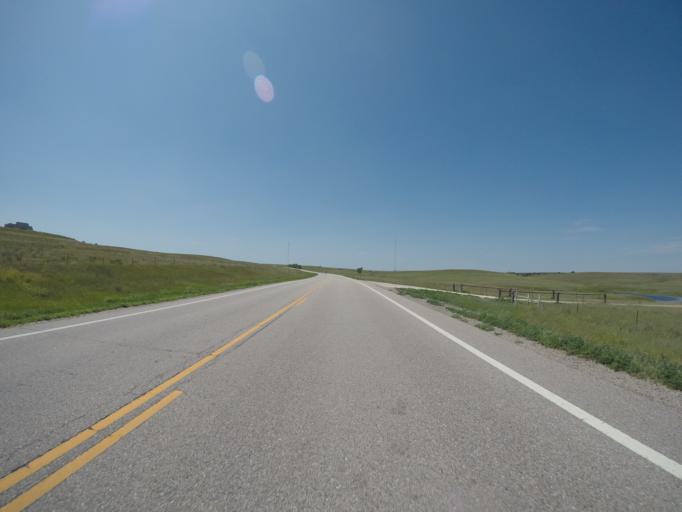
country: US
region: Kansas
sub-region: Osborne County
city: Osborne
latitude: 39.4914
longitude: -98.6964
